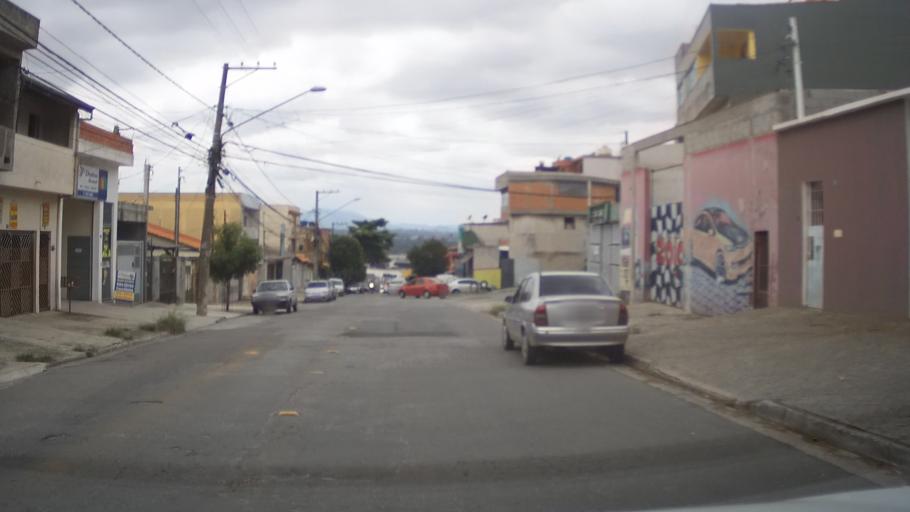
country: BR
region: Sao Paulo
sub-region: Itaquaquecetuba
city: Itaquaquecetuba
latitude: -23.4314
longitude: -46.4346
